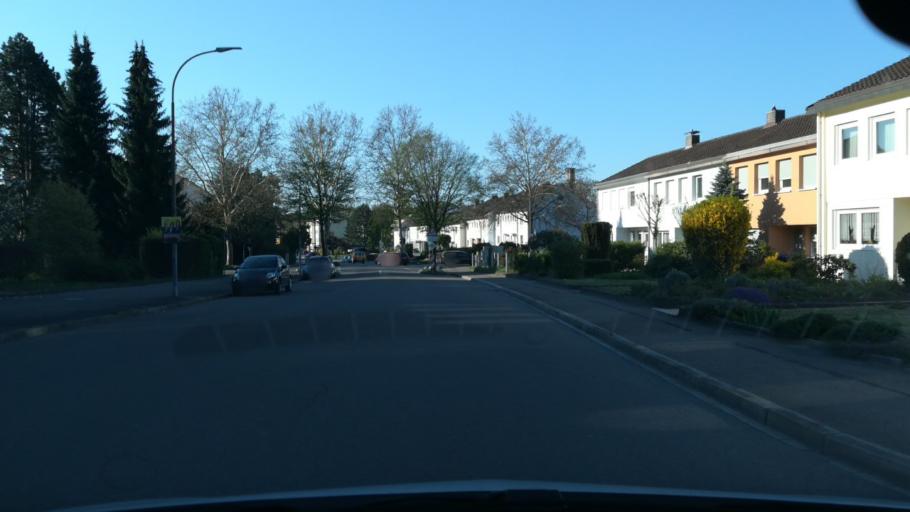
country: DE
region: Baden-Wuerttemberg
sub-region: Freiburg Region
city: Singen
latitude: 47.7723
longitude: 8.8392
